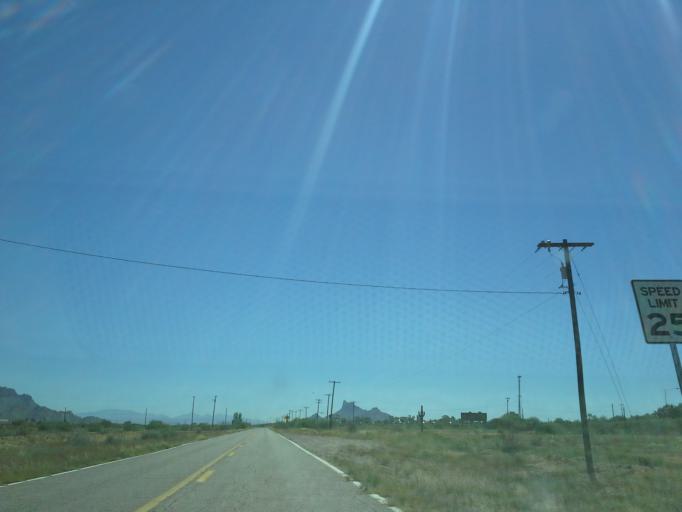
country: US
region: Arizona
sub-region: Pinal County
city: Eloy
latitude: 32.7209
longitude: -111.5093
